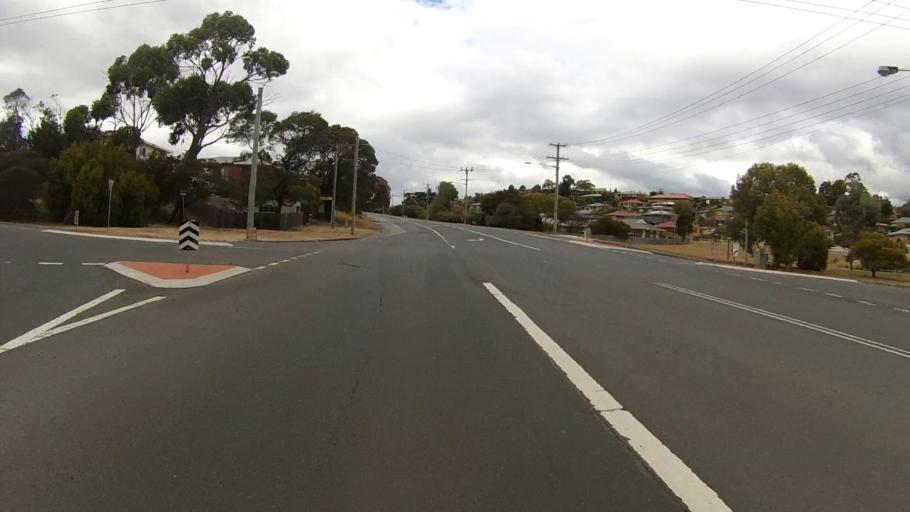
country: AU
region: Tasmania
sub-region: Glenorchy
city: Austins Ferry
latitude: -42.7658
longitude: 147.2432
